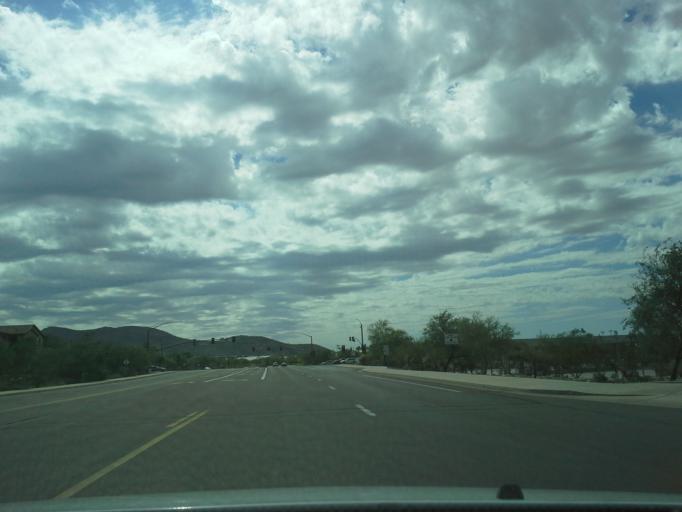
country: US
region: Arizona
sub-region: Maricopa County
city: Scottsdale
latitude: 33.6305
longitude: -111.8649
